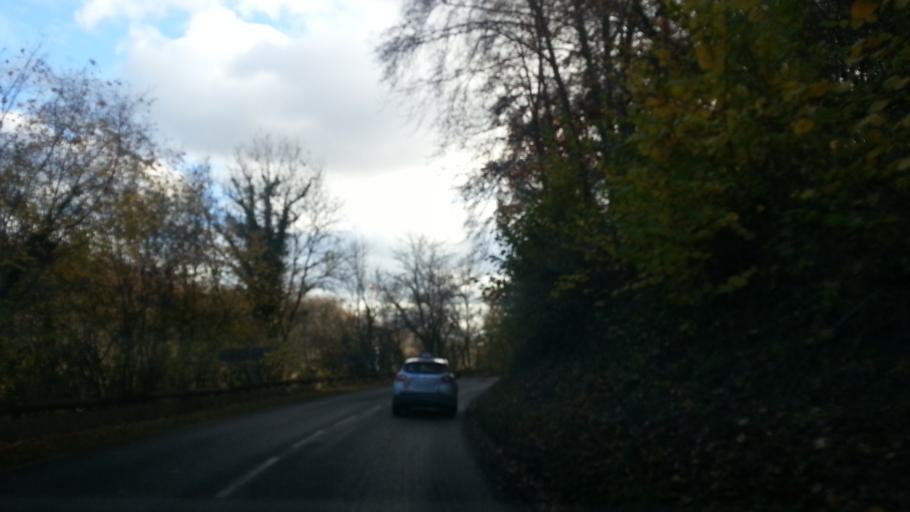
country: FR
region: Picardie
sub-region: Departement de l'Oise
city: Verneuil-en-Halatte
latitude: 49.2619
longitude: 2.5408
